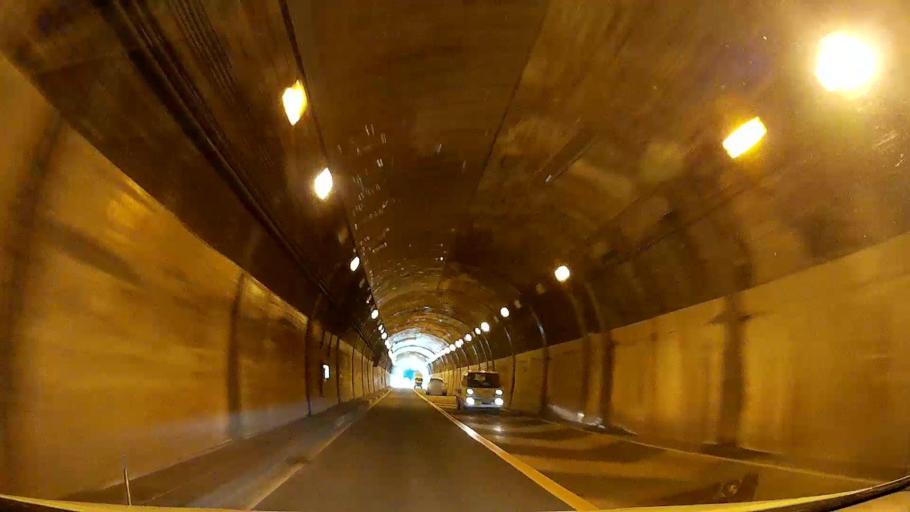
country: JP
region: Shizuoka
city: Atami
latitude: 35.0869
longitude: 139.0787
